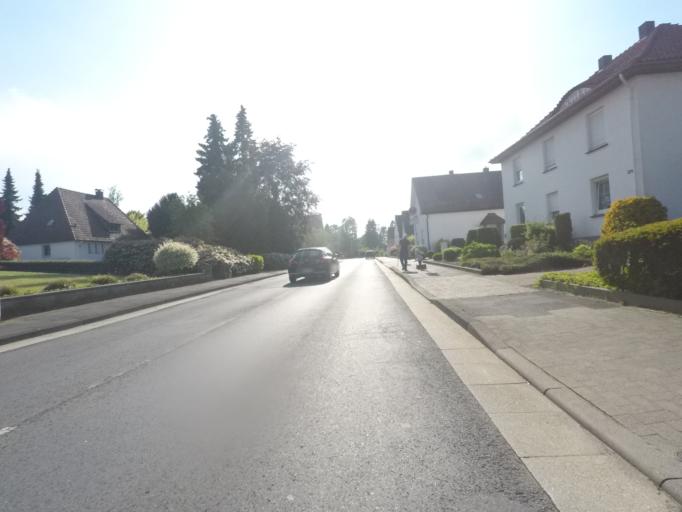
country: DE
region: North Rhine-Westphalia
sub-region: Regierungsbezirk Detmold
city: Hiddenhausen
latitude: 52.1650
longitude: 8.6282
